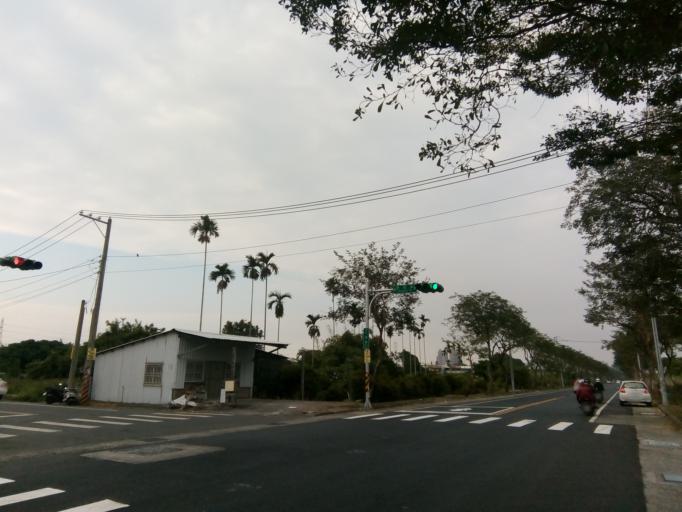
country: TW
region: Taiwan
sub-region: Chiayi
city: Jiayi Shi
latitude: 23.4545
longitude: 120.4704
